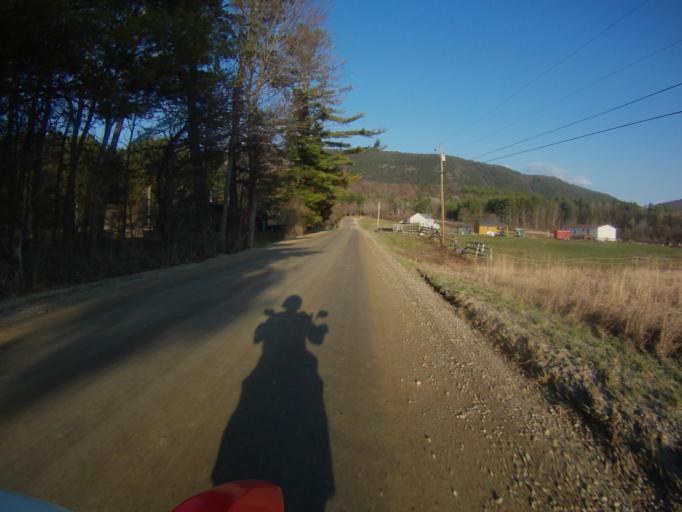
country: US
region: Vermont
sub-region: Addison County
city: Bristol
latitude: 44.0974
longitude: -73.0901
